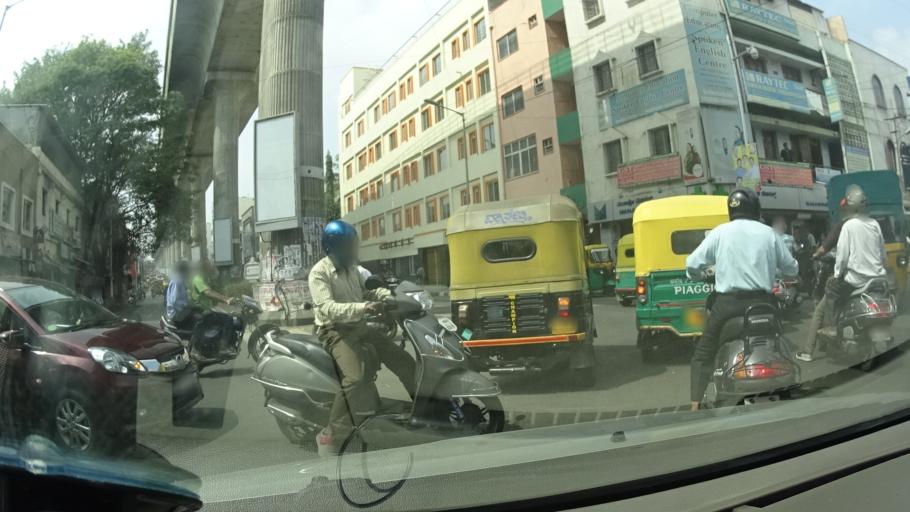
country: IN
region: Karnataka
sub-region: Bangalore Urban
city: Bangalore
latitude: 12.9987
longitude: 77.5555
